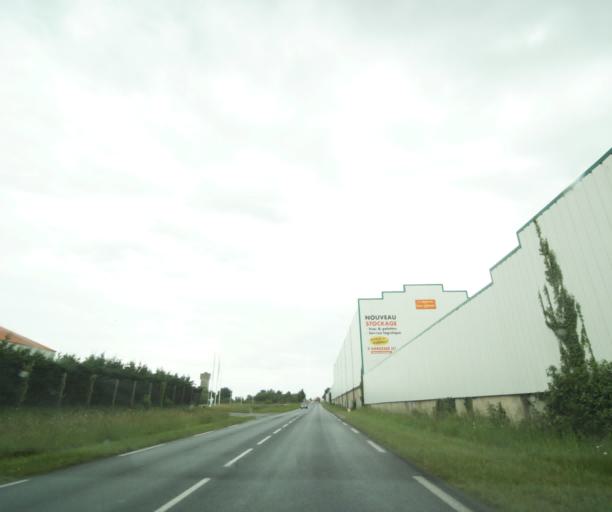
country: FR
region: Poitou-Charentes
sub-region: Departement des Deux-Sevres
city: Chatillon-sur-Thouet
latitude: 46.6692
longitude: -0.2463
